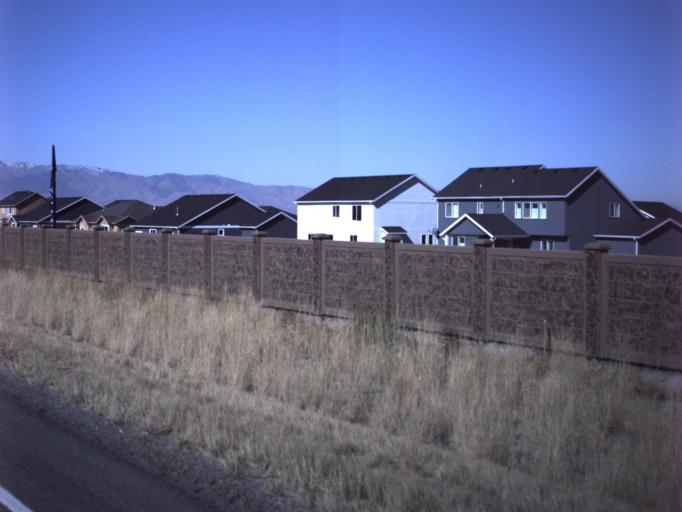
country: US
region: Utah
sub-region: Tooele County
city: Stansbury park
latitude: 40.6450
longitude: -112.3080
